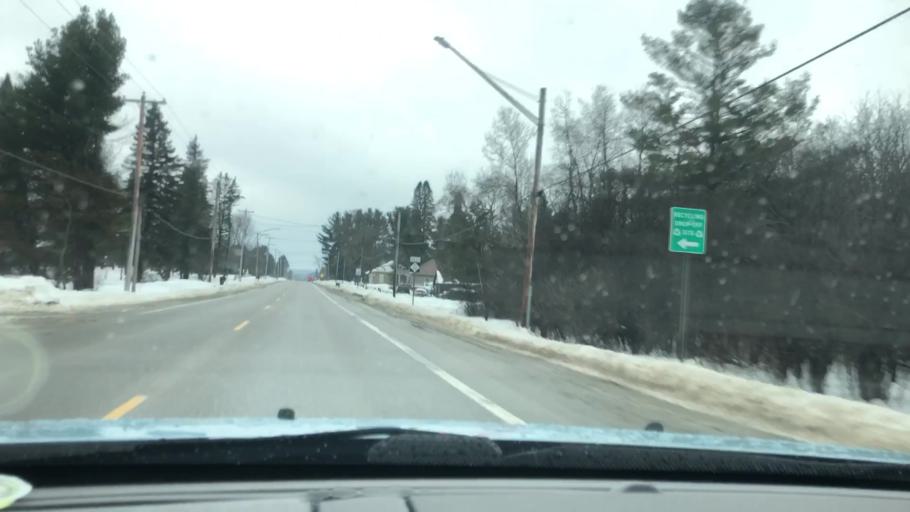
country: US
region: Michigan
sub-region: Charlevoix County
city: East Jordan
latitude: 45.1477
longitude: -85.1192
